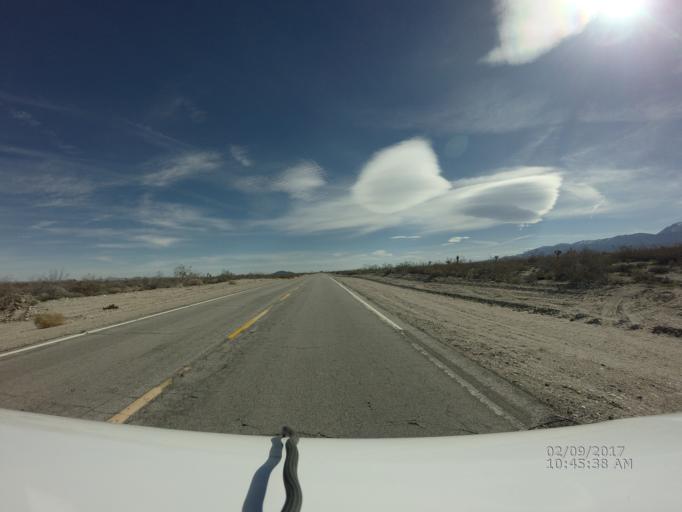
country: US
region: California
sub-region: Los Angeles County
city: Lake Los Angeles
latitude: 34.5427
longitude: -117.8676
